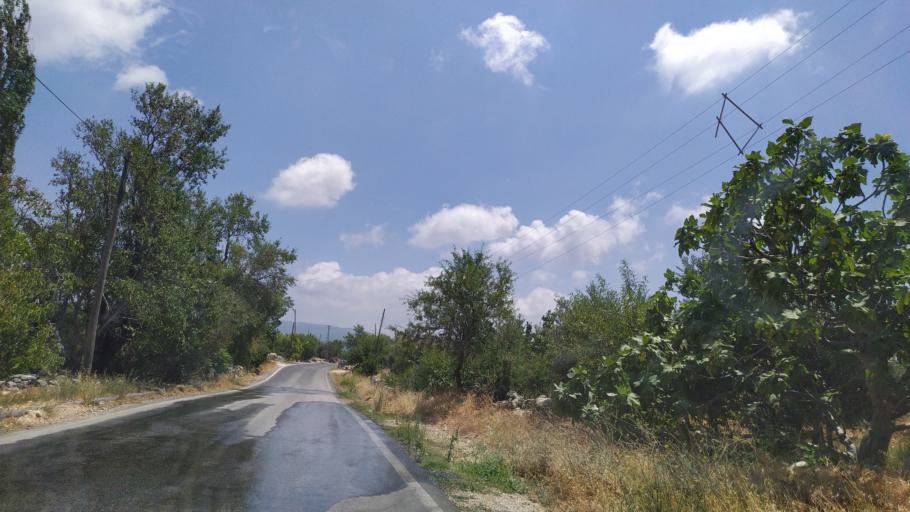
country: TR
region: Mersin
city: Gulnar
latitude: 36.2844
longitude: 33.3855
